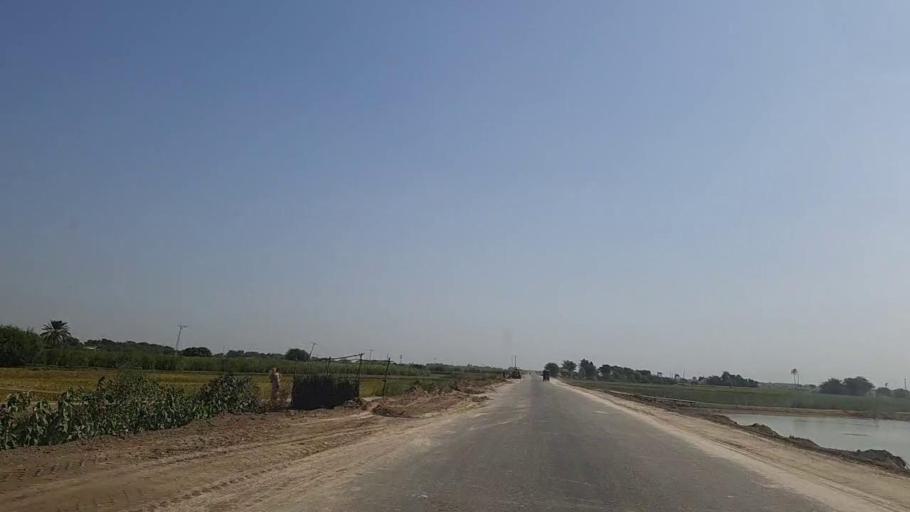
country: PK
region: Sindh
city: Mirpur Batoro
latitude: 24.7521
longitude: 68.2333
